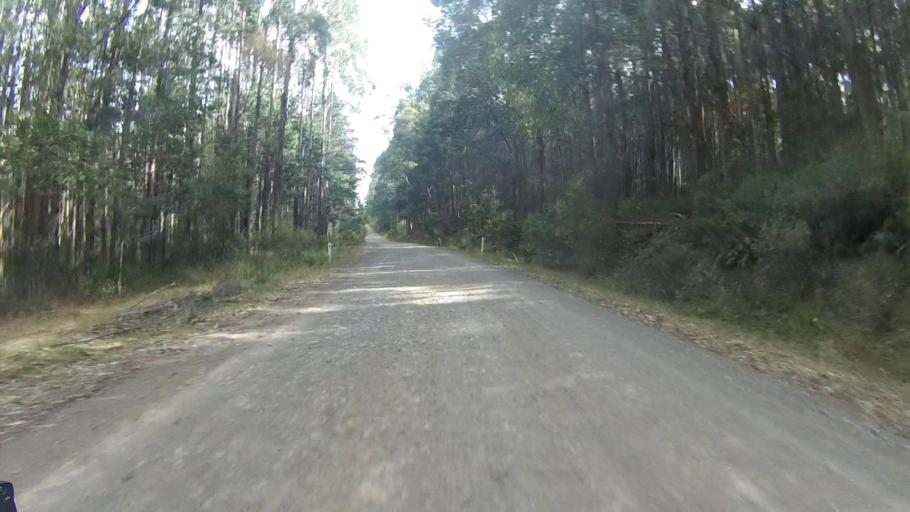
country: AU
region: Tasmania
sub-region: Sorell
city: Sorell
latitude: -42.7470
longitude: 147.8291
